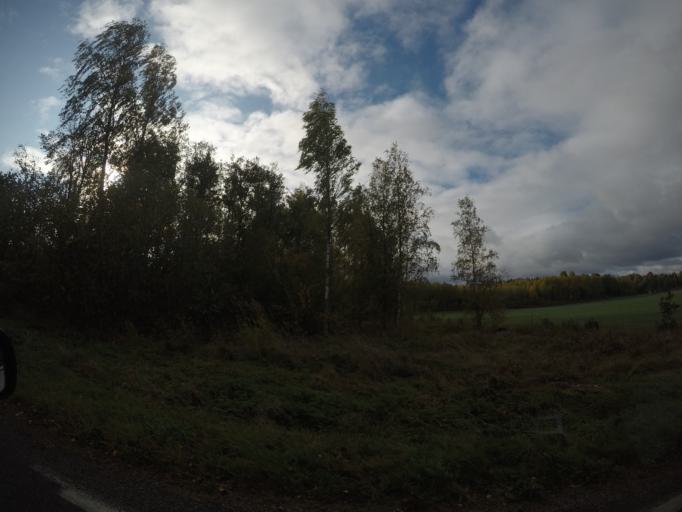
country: SE
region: Soedermanland
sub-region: Eskilstuna Kommun
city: Kvicksund
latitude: 59.3340
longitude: 16.2523
